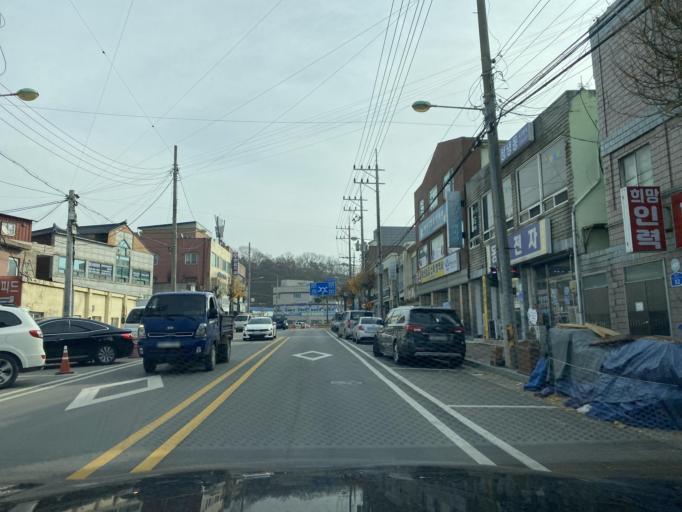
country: KR
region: Chungcheongnam-do
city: Yesan
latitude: 36.6819
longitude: 126.8317
